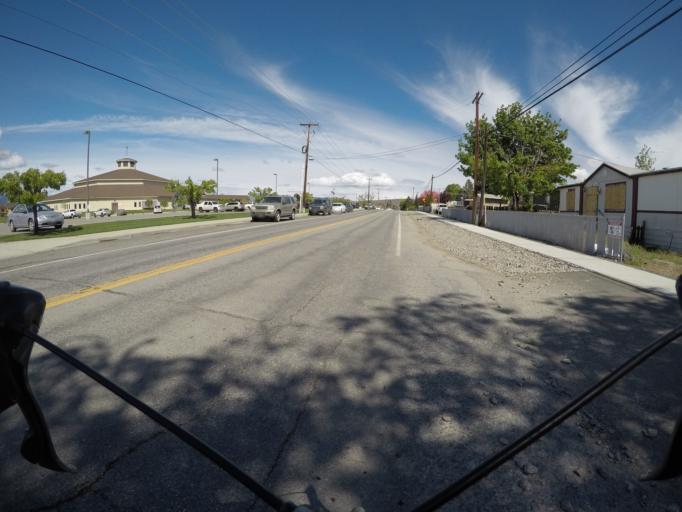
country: US
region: Washington
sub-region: Chelan County
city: South Wenatchee
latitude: 47.3970
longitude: -120.2603
